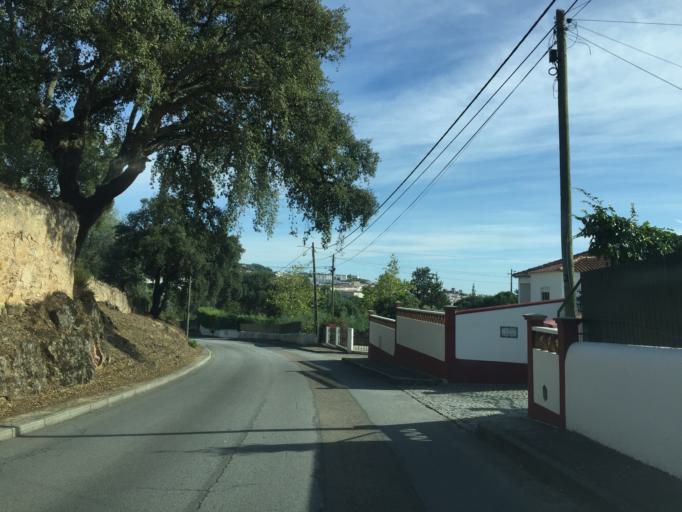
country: PT
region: Portalegre
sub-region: Portalegre
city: Portalegre
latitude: 39.3075
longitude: -7.4385
